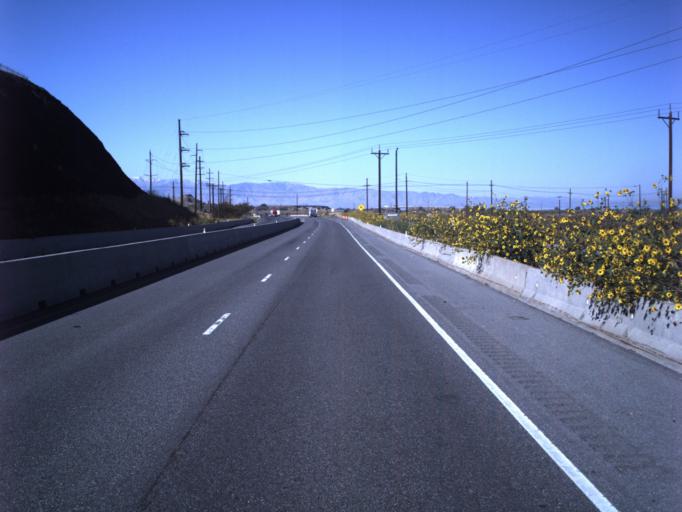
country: US
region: Utah
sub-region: Salt Lake County
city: Magna
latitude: 40.7268
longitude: -112.1980
